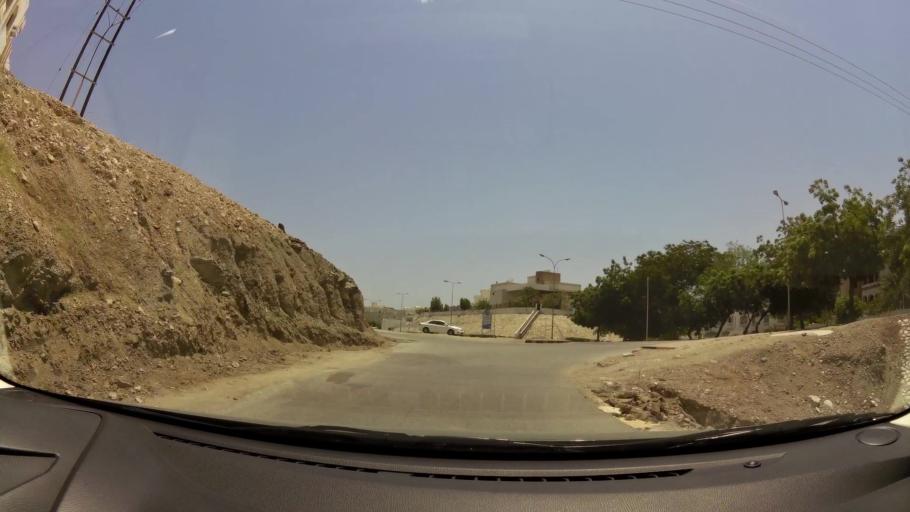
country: OM
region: Muhafazat Masqat
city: Muscat
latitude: 23.6093
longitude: 58.5385
